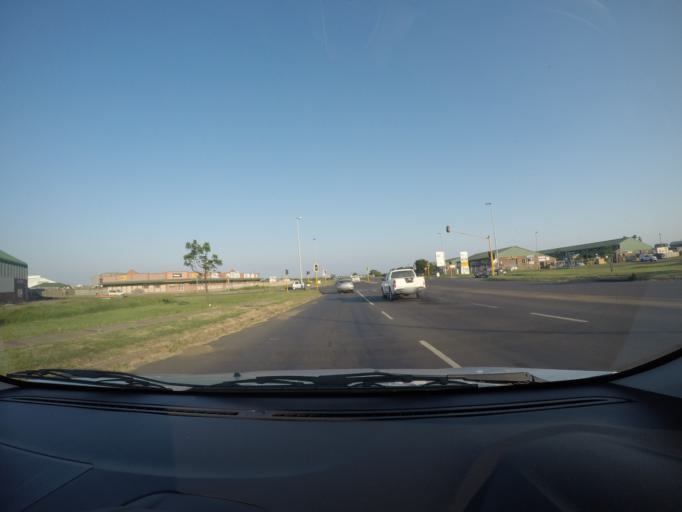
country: ZA
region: KwaZulu-Natal
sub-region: uThungulu District Municipality
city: Richards Bay
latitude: -28.7520
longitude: 32.0309
